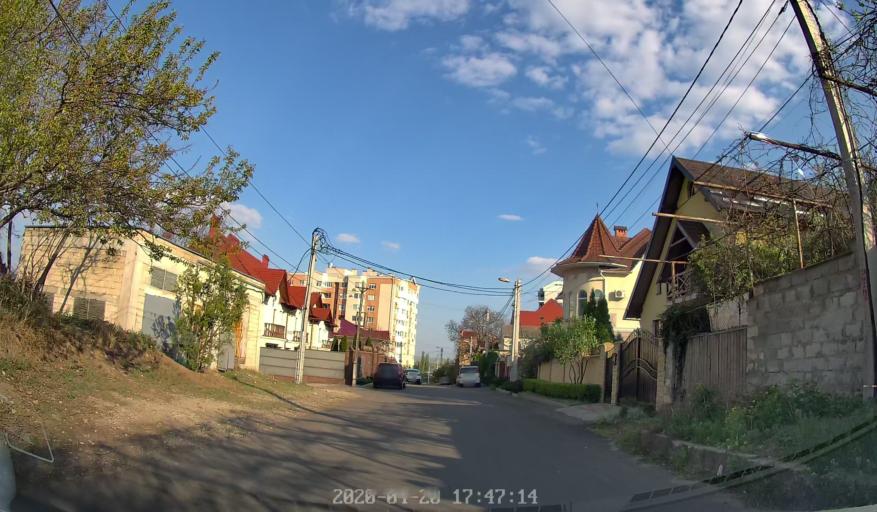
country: MD
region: Chisinau
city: Chisinau
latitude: 47.0038
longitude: 28.8639
